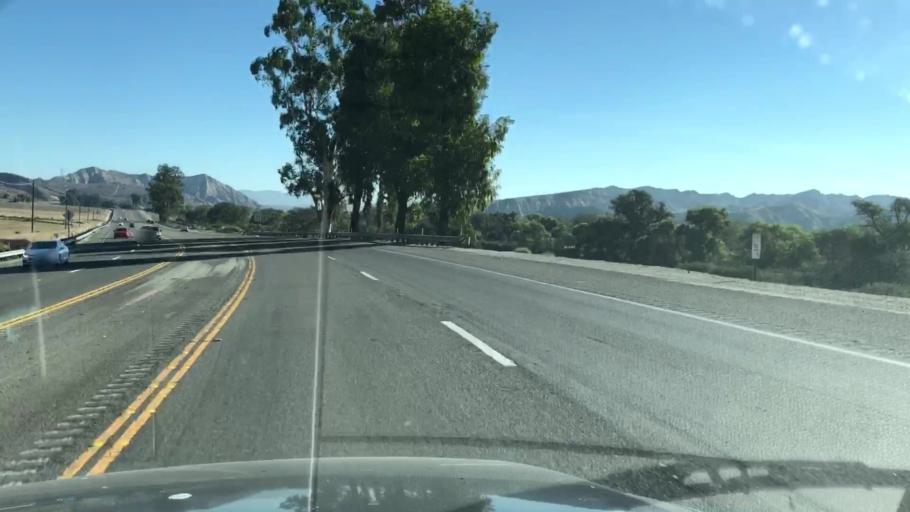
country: US
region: California
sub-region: Los Angeles County
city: Val Verde
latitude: 34.4112
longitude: -118.6681
